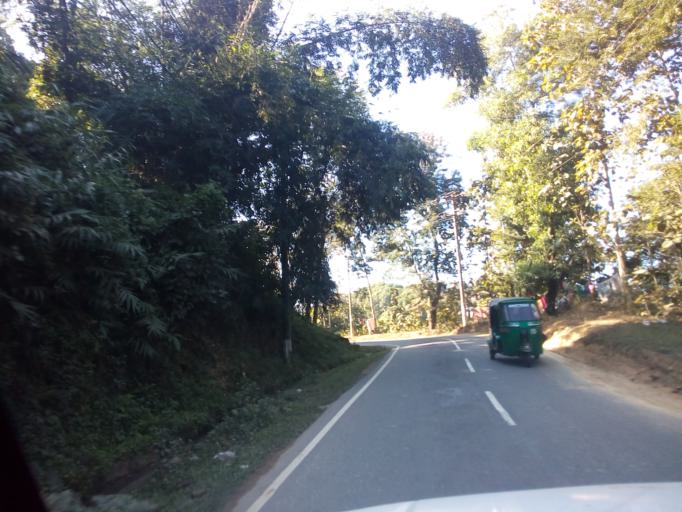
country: BD
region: Chittagong
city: Bandarban
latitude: 22.1851
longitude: 92.2097
